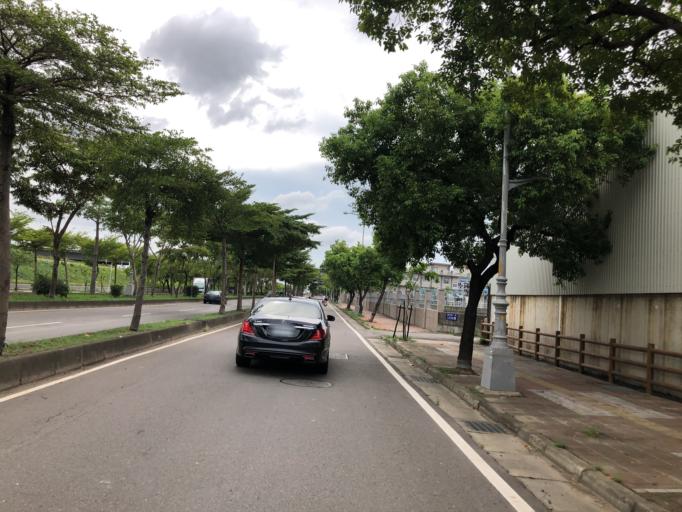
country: TW
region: Taiwan
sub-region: Taichung City
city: Taichung
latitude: 24.0913
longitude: 120.6508
